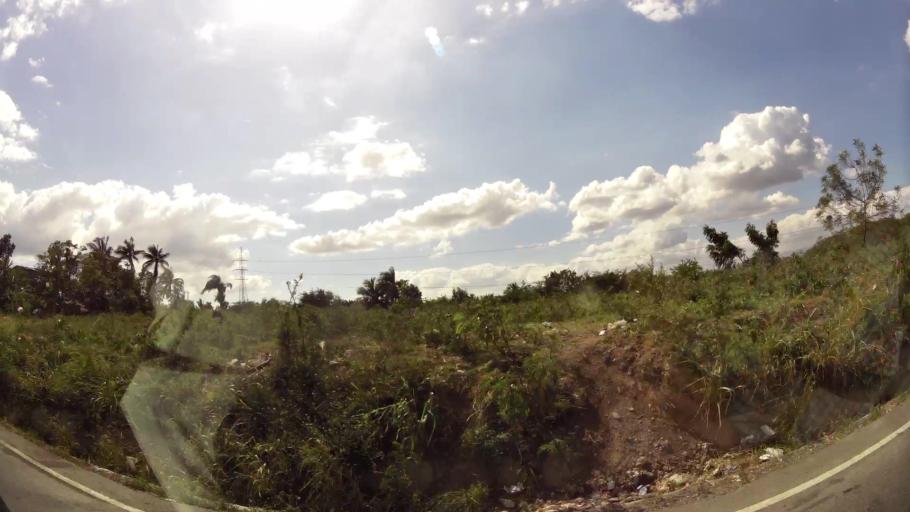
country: DO
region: San Cristobal
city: Bajos de Haina
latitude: 18.4249
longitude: -70.0408
